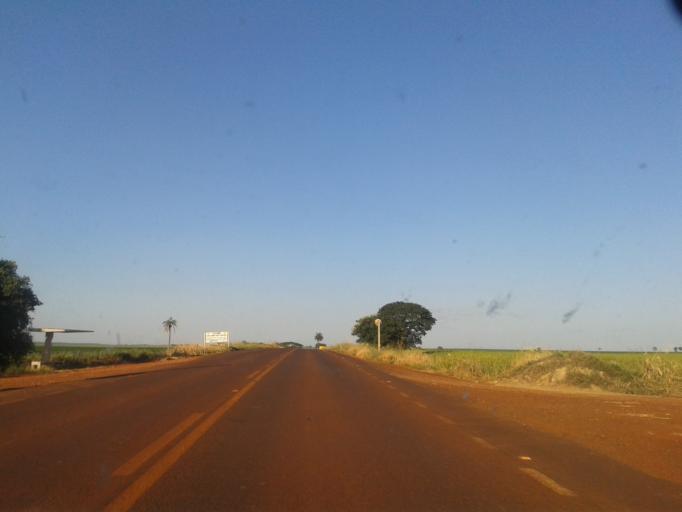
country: BR
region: Minas Gerais
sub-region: Capinopolis
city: Capinopolis
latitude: -18.7095
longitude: -49.7134
